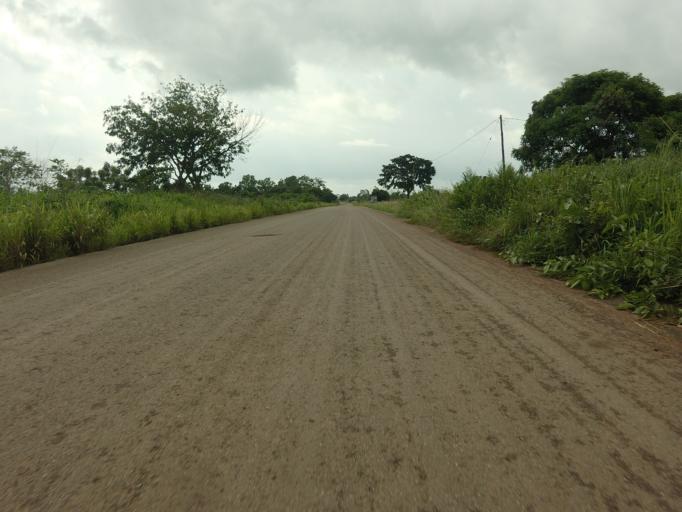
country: GH
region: Volta
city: Kpandu
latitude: 6.9444
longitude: 0.4608
